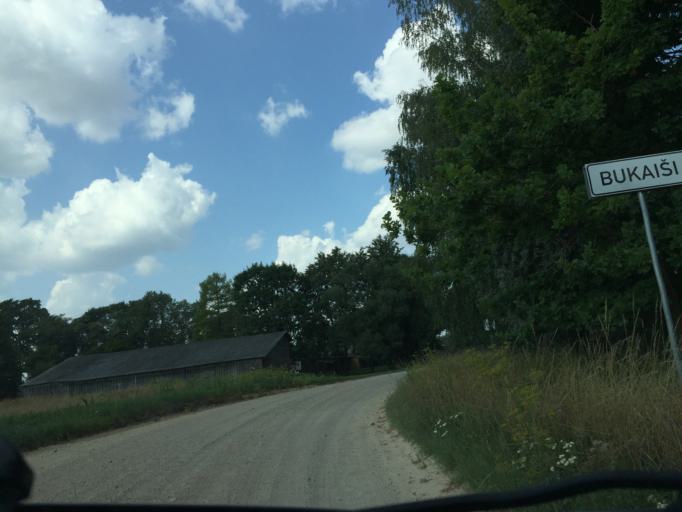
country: LT
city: Zagare
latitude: 56.3973
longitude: 23.2513
